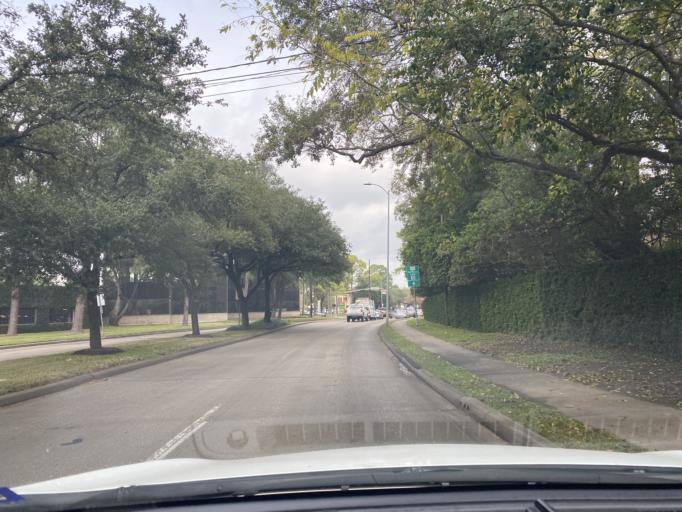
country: US
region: Texas
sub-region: Harris County
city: Hunters Creek Village
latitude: 29.7627
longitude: -95.4776
